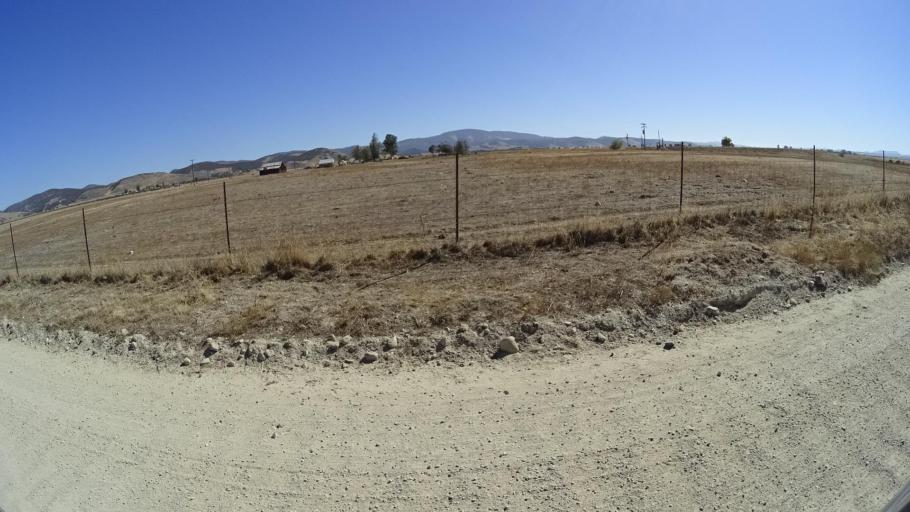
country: US
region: California
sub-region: Monterey County
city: King City
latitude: 35.9577
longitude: -121.1002
